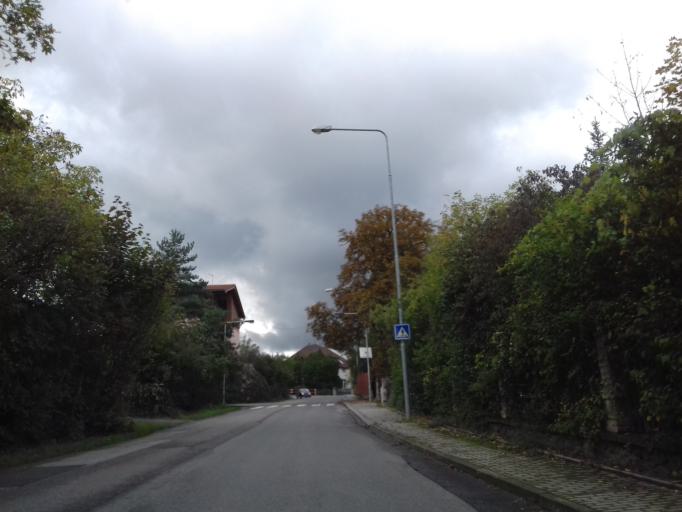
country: CZ
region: Central Bohemia
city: Cernosice
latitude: 49.9556
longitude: 14.3215
